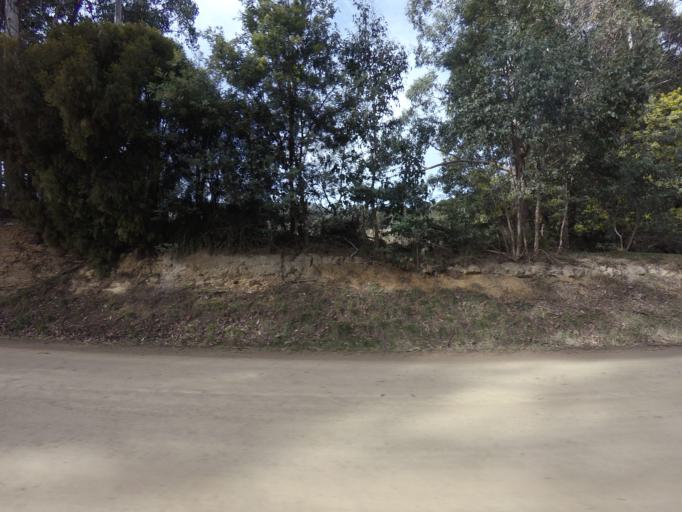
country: AU
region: Tasmania
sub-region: Huon Valley
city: Huonville
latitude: -43.0749
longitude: 147.0752
